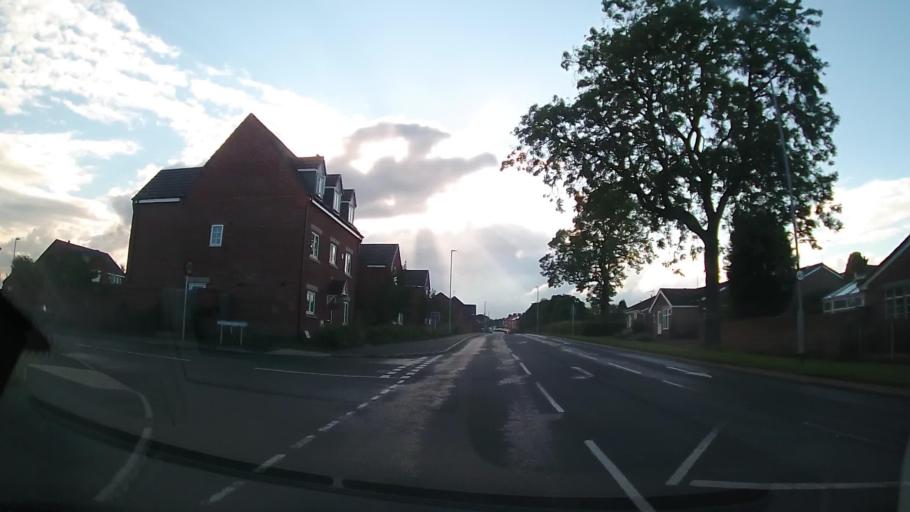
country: GB
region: England
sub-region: Leicestershire
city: Markfield
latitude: 52.6818
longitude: -1.2754
